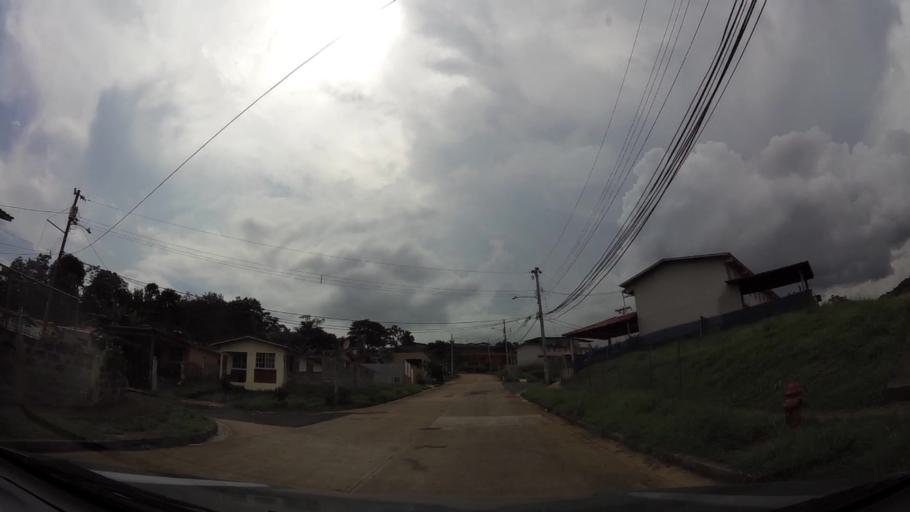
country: PA
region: Panama
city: Tocumen
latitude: 9.1097
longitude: -79.3789
